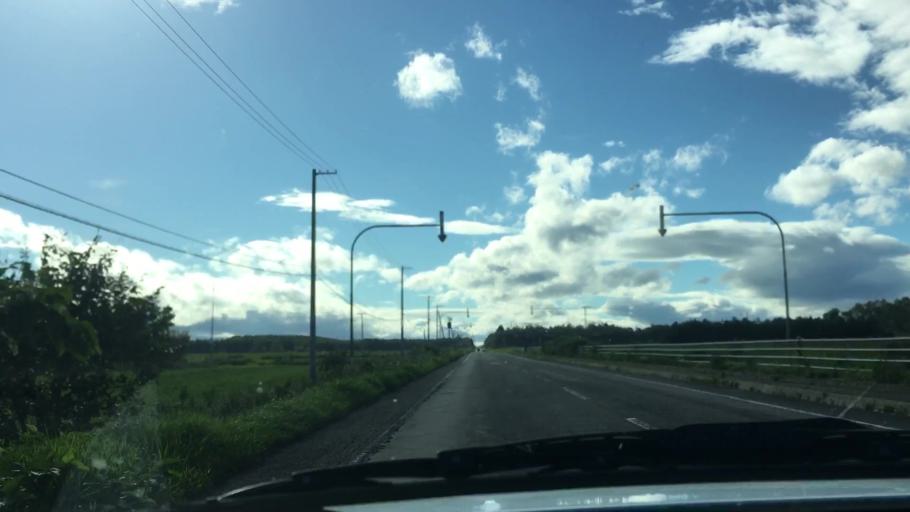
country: JP
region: Hokkaido
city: Otofuke
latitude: 43.1600
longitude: 143.1661
